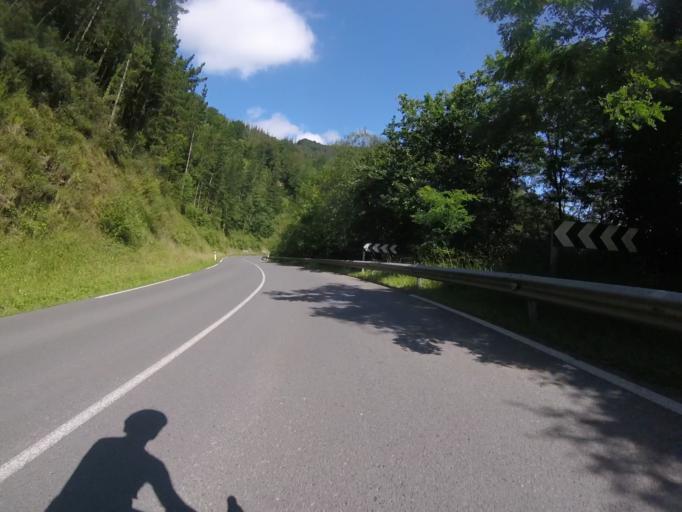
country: ES
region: Basque Country
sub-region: Provincia de Guipuzcoa
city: Beizama
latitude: 43.1147
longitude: -2.2282
